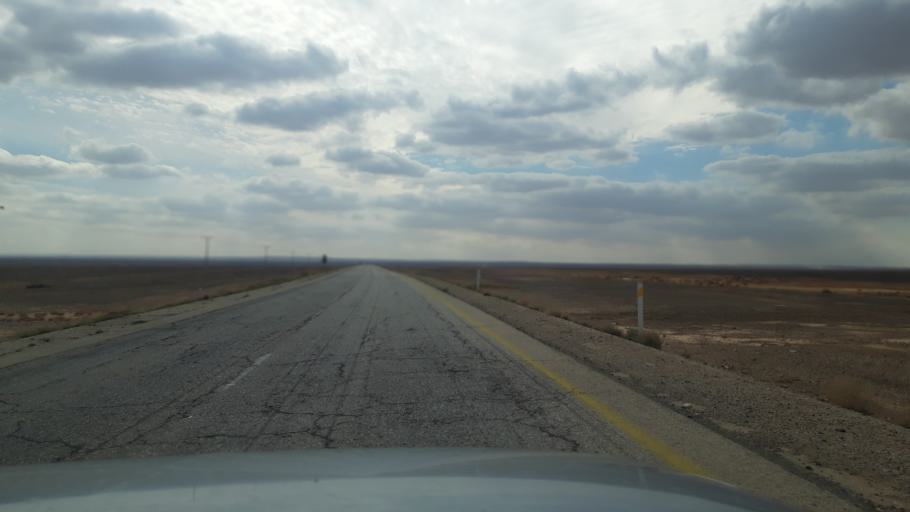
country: JO
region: Amman
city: Al Azraq ash Shamali
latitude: 31.8429
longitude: 36.6470
